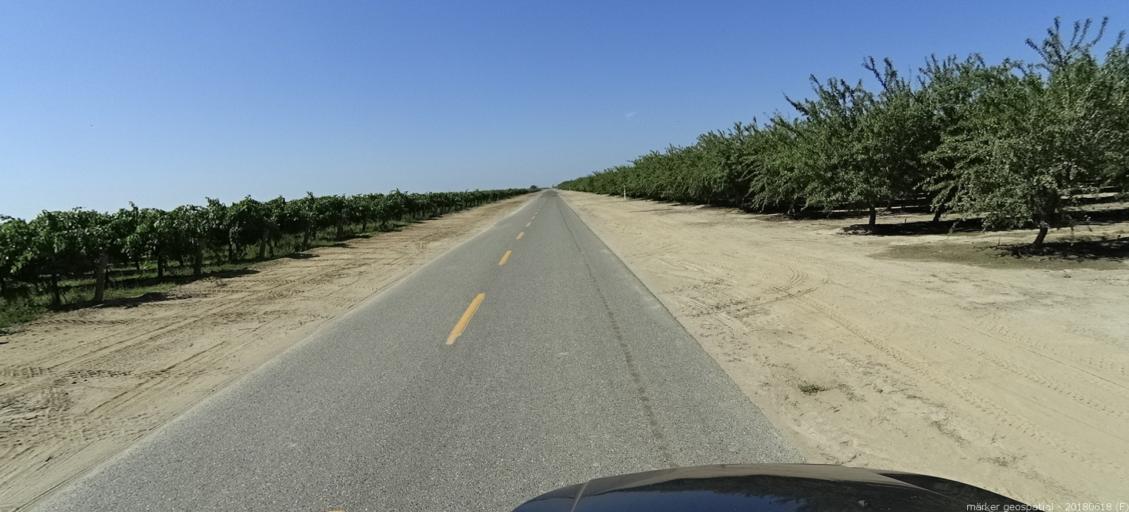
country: US
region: California
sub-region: Madera County
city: Parkwood
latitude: 36.8644
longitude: -120.1465
